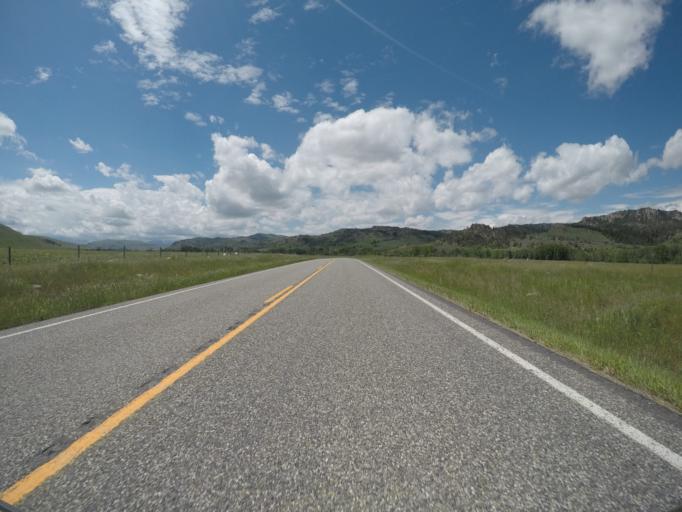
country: US
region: Montana
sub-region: Sweet Grass County
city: Big Timber
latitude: 45.6901
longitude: -110.0537
